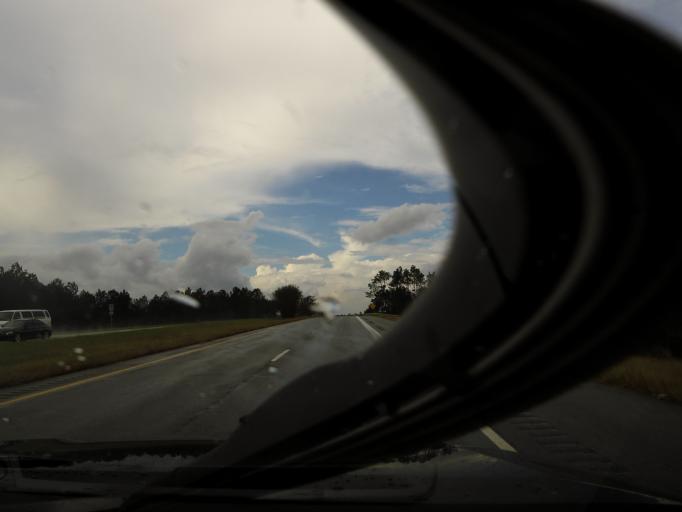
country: US
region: Georgia
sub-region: Wayne County
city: Jesup
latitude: 31.6188
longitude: -81.8643
